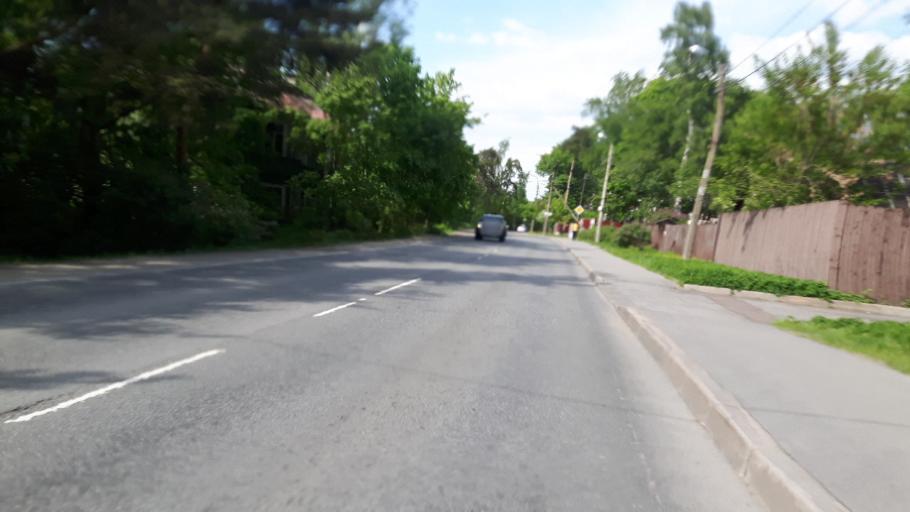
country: RU
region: Leningrad
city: Gorskaya
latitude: 60.0467
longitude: 29.9769
